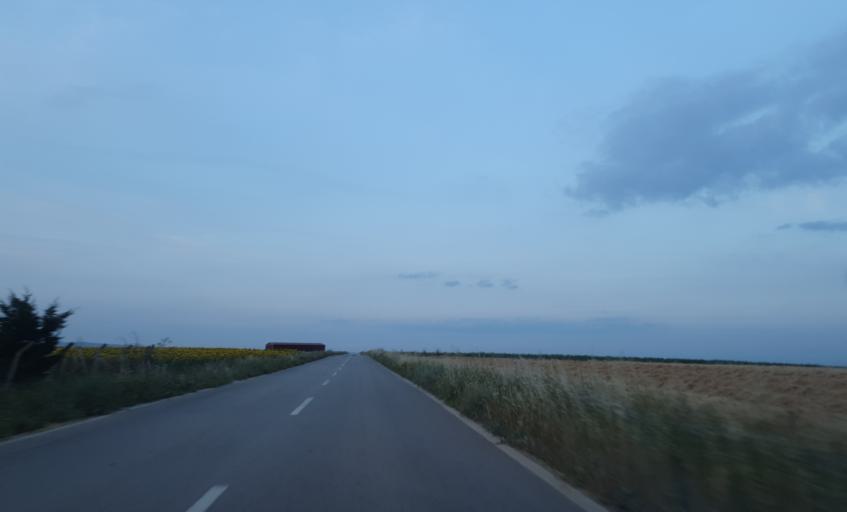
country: TR
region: Tekirdag
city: Beyazkoy
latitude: 41.4191
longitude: 27.6662
